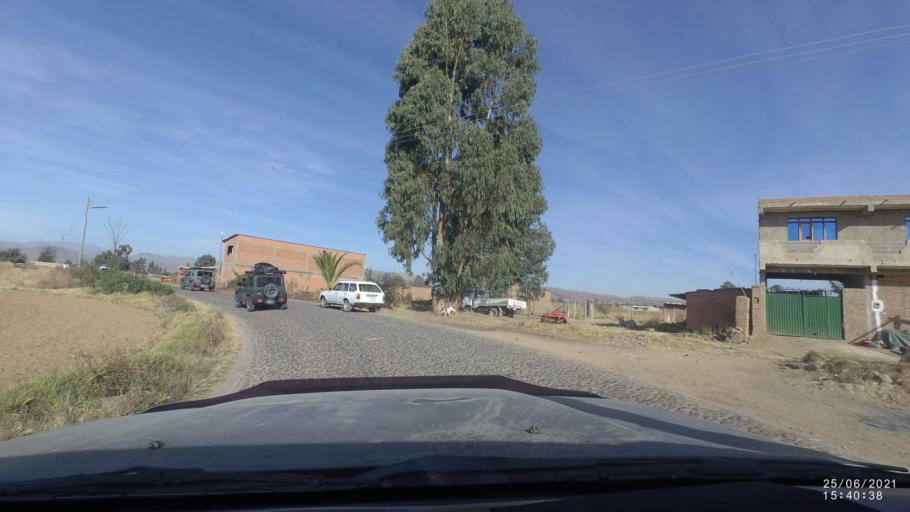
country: BO
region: Cochabamba
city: Cliza
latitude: -17.6317
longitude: -65.9235
